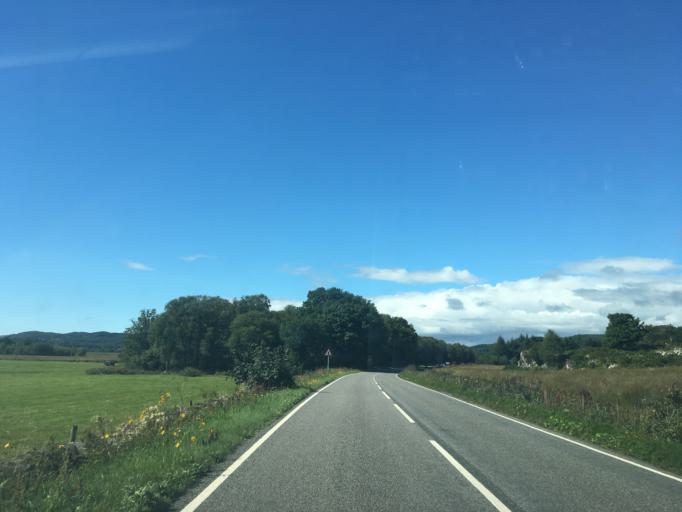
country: GB
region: Scotland
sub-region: Argyll and Bute
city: Lochgilphead
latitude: 56.0919
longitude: -5.4723
